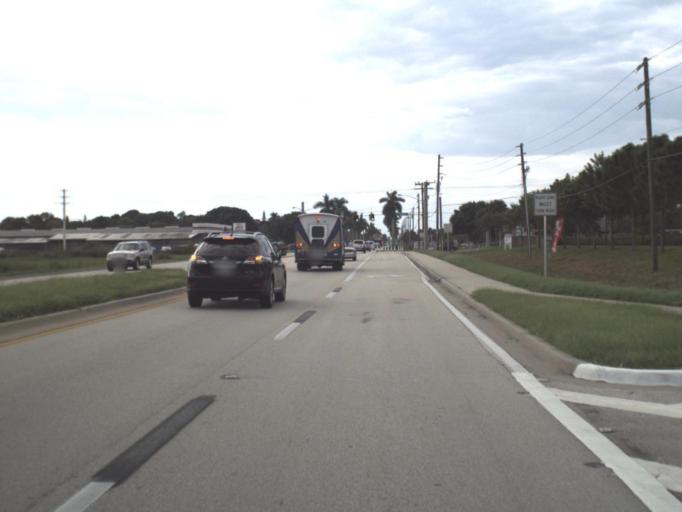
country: US
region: Florida
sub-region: Lee County
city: Harlem Heights
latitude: 26.5105
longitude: -81.9438
